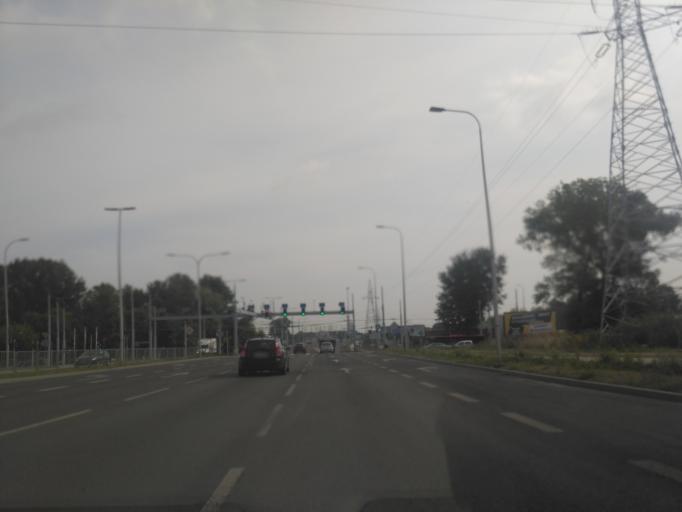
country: PL
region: Lublin Voivodeship
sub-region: Powiat lubelski
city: Lublin
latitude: 51.2316
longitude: 22.5603
